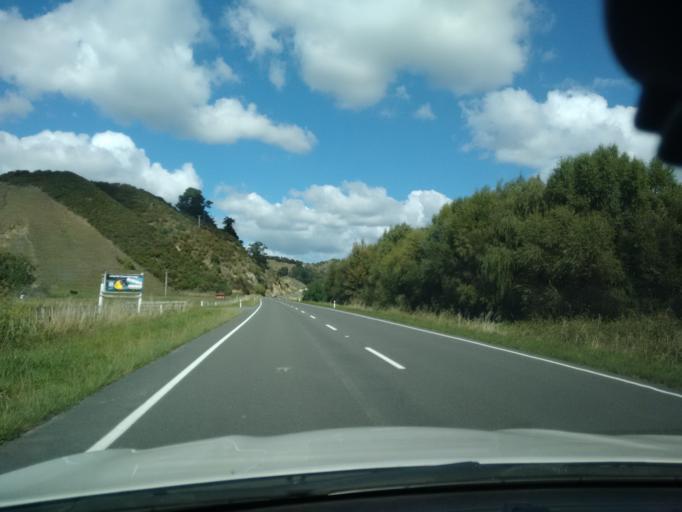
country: NZ
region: Manawatu-Wanganui
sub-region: Wanganui District
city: Wanganui
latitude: -39.8862
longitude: 175.1057
